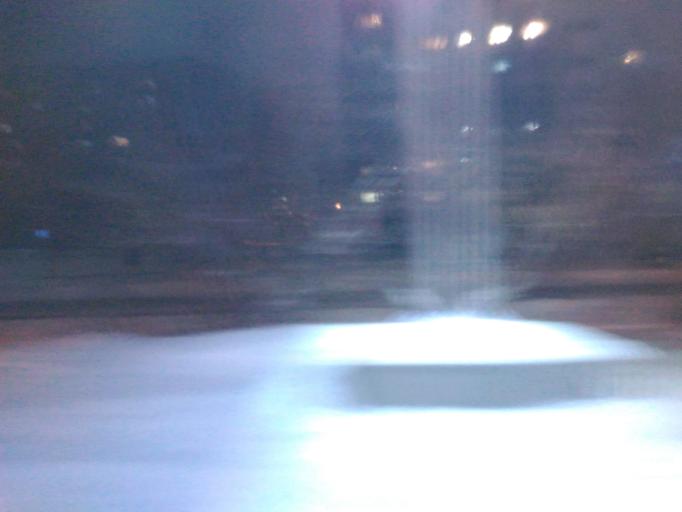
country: RU
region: Ulyanovsk
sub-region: Ulyanovskiy Rayon
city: Ulyanovsk
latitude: 54.3222
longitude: 48.3571
